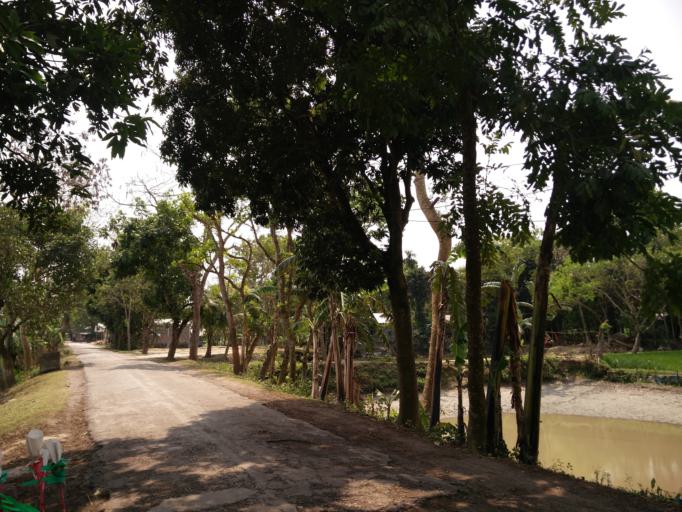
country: BD
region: Dhaka
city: Sherpur
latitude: 24.9472
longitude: 90.1606
